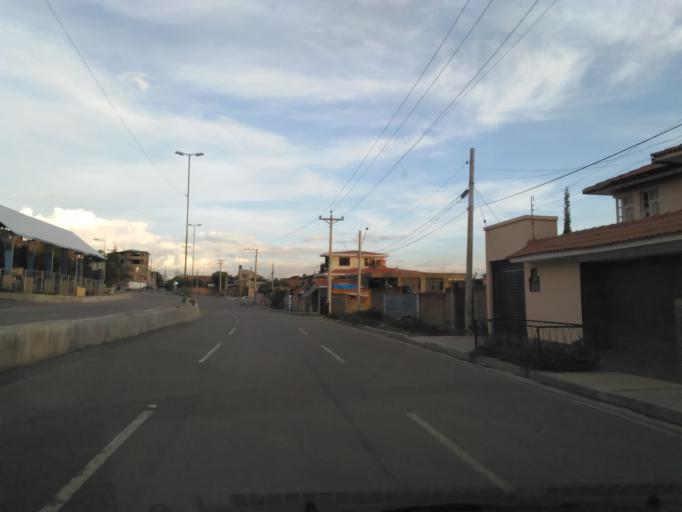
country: BO
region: Cochabamba
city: Cochabamba
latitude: -17.3502
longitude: -66.1704
